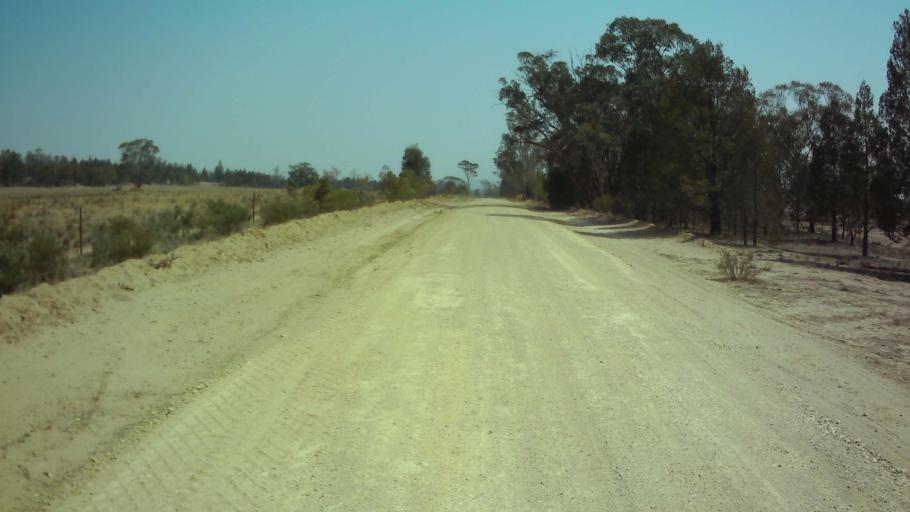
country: AU
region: New South Wales
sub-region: Weddin
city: Grenfell
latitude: -33.6560
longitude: 148.2734
